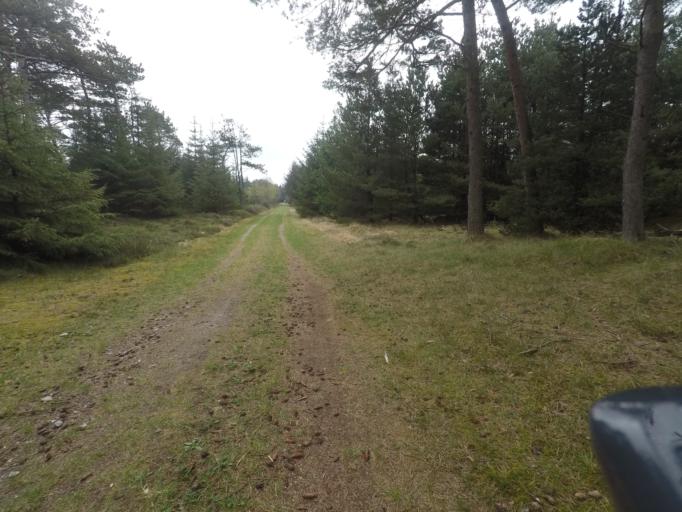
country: DE
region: Schleswig-Holstein
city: List
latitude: 55.1041
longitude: 8.5232
